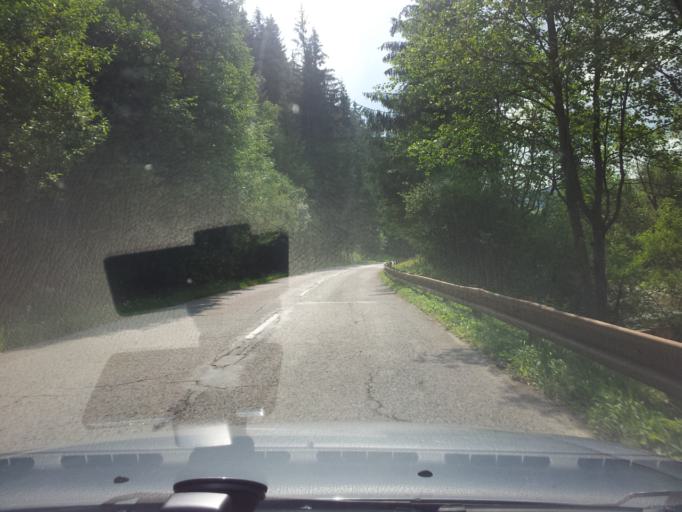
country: SK
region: Zilinsky
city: Oravska Lesna
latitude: 49.3822
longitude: 19.2372
